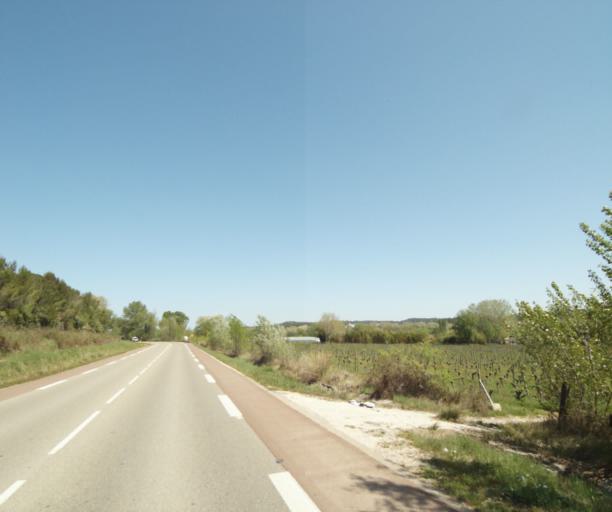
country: FR
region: Languedoc-Roussillon
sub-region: Departement de l'Herault
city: Montferrier-sur-Lez
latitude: 43.6798
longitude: 3.8567
